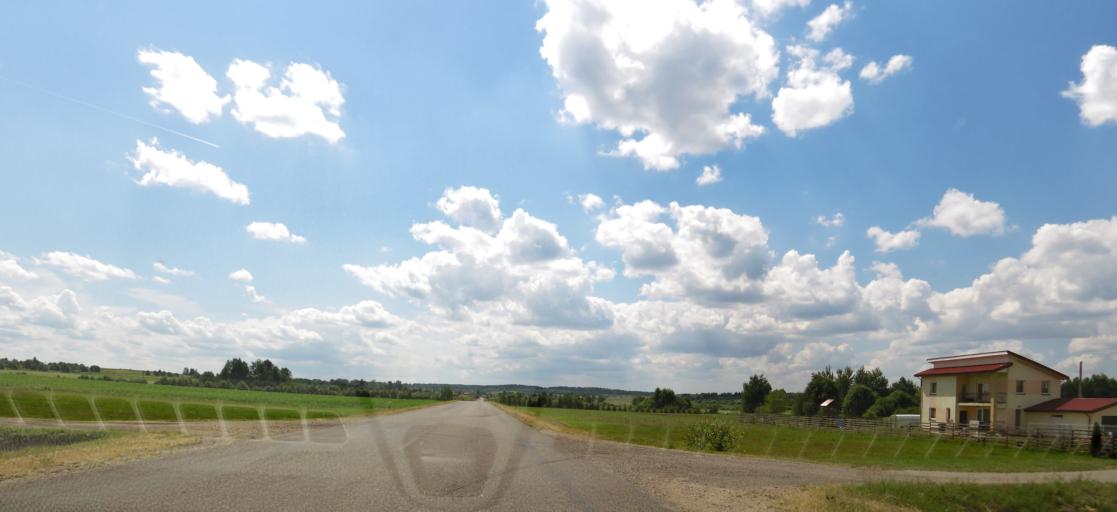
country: LT
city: Skaidiskes
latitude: 54.5533
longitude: 25.6610
